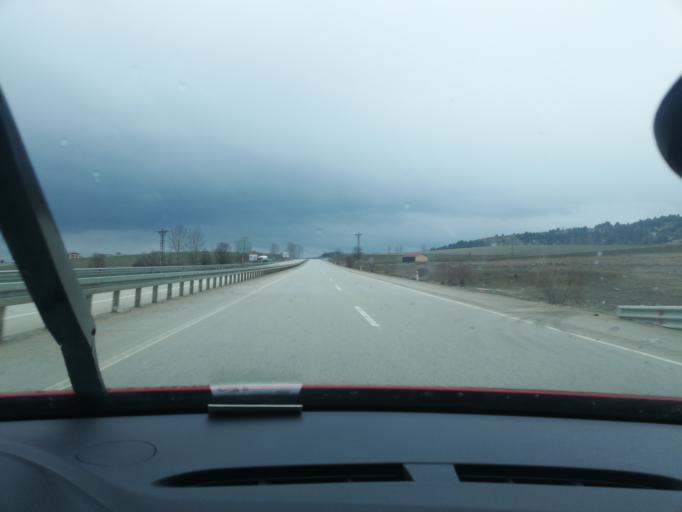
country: TR
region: Kastamonu
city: Seydiler
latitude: 41.6139
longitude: 33.7280
